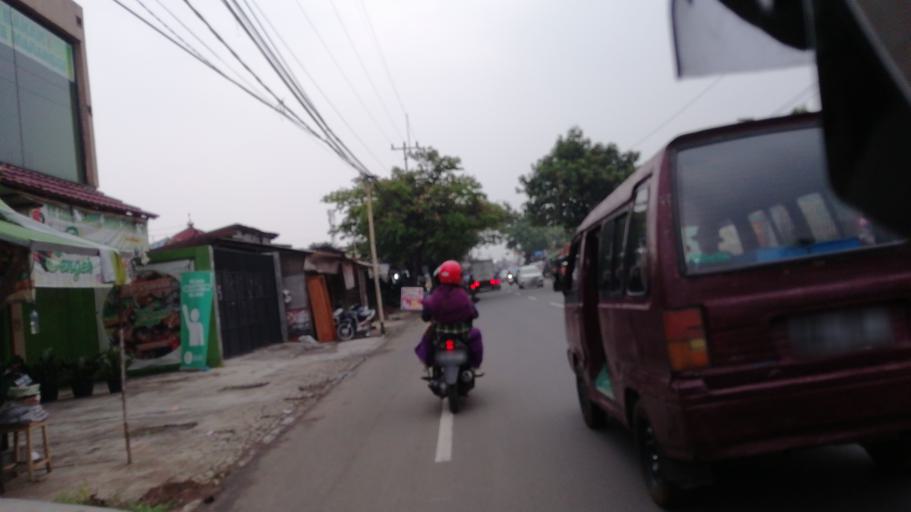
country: ID
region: West Java
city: Cibinong
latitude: -6.5152
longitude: 106.8078
